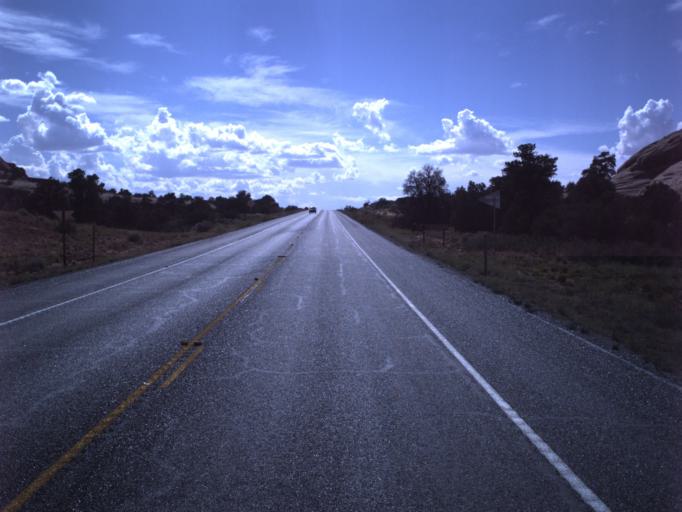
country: US
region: Utah
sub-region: Grand County
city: Moab
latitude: 38.6440
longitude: -109.7379
